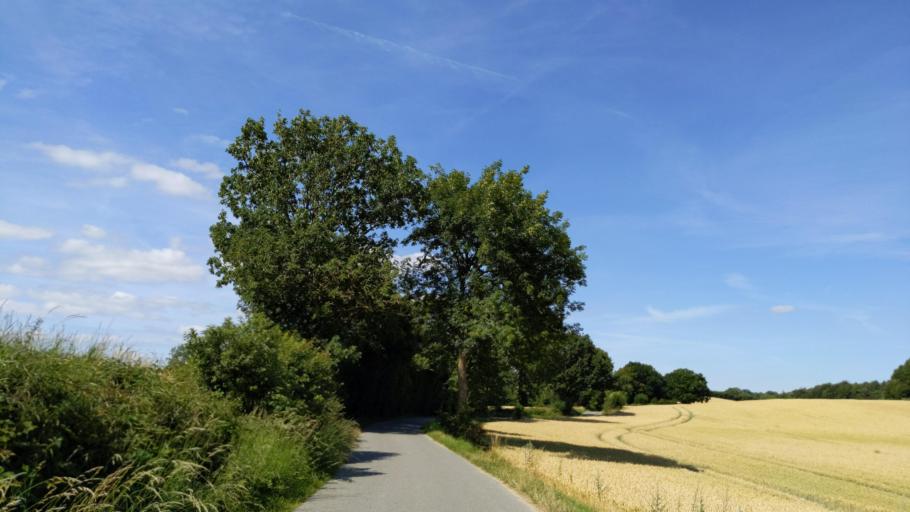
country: DE
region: Schleswig-Holstein
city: Kasseedorf
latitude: 54.1352
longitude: 10.7384
